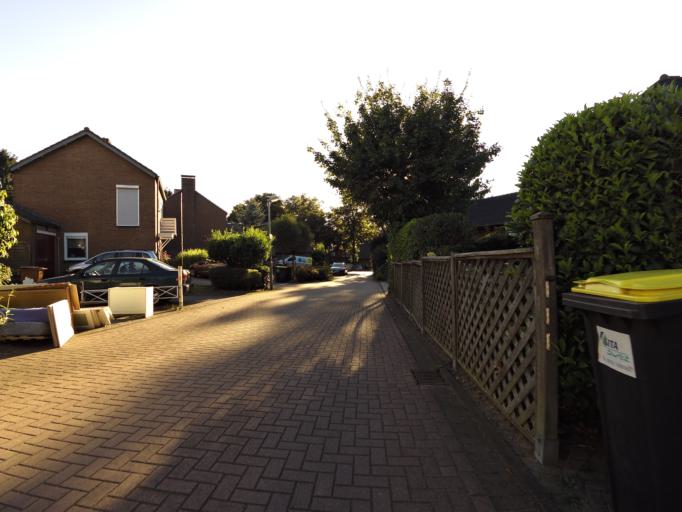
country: DE
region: North Rhine-Westphalia
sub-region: Regierungsbezirk Dusseldorf
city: Kleve
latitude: 51.8699
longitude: 6.1647
